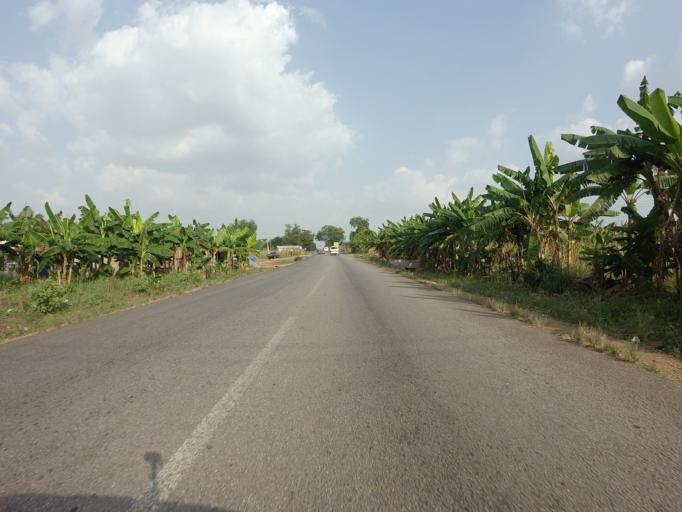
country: GH
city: Akropong
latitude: 6.2431
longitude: 0.1213
